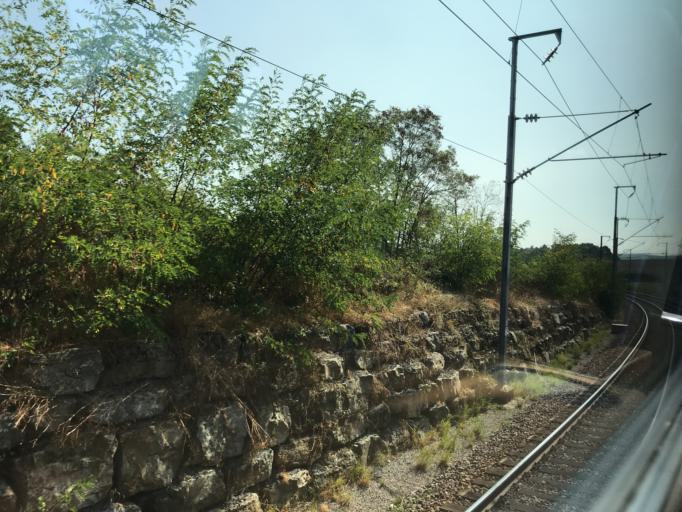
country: LU
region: Luxembourg
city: Belvaux
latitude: 49.5025
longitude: 5.9248
